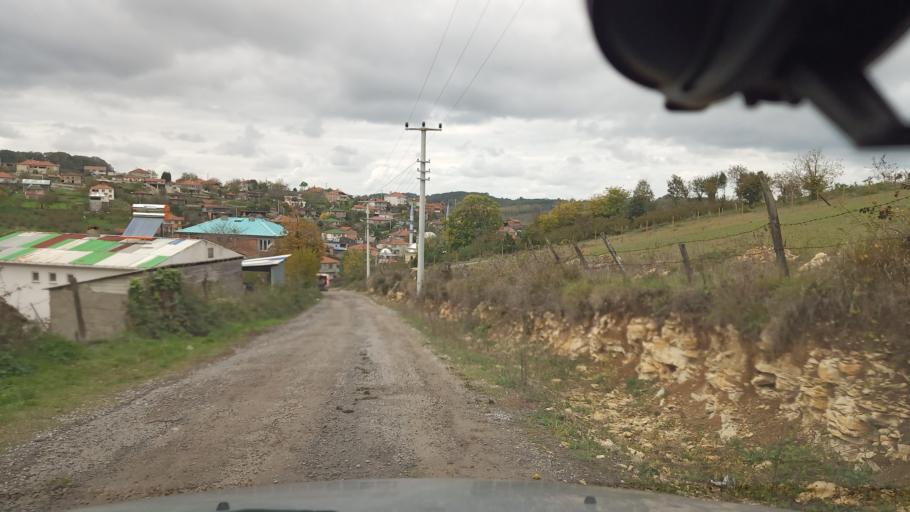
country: TR
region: Sakarya
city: Karasu
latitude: 41.0915
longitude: 30.5851
